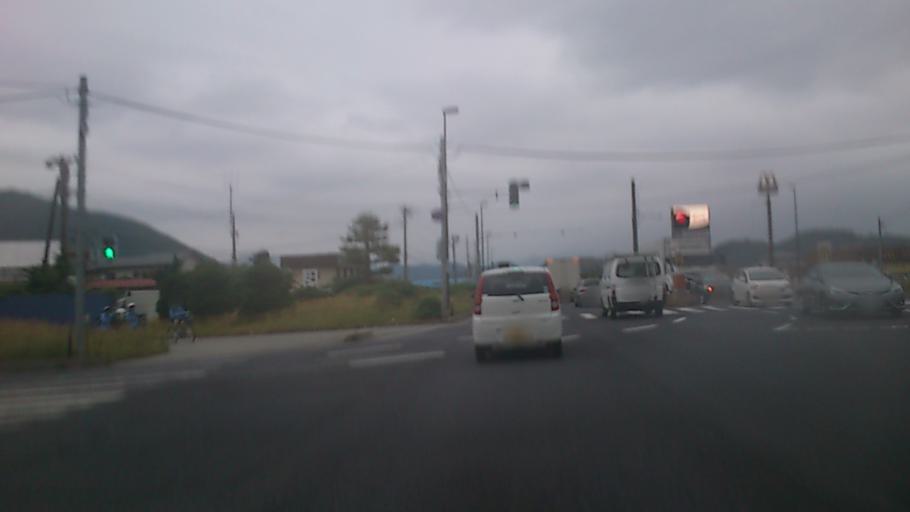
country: JP
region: Yamagata
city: Tendo
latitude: 38.3743
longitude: 140.3831
